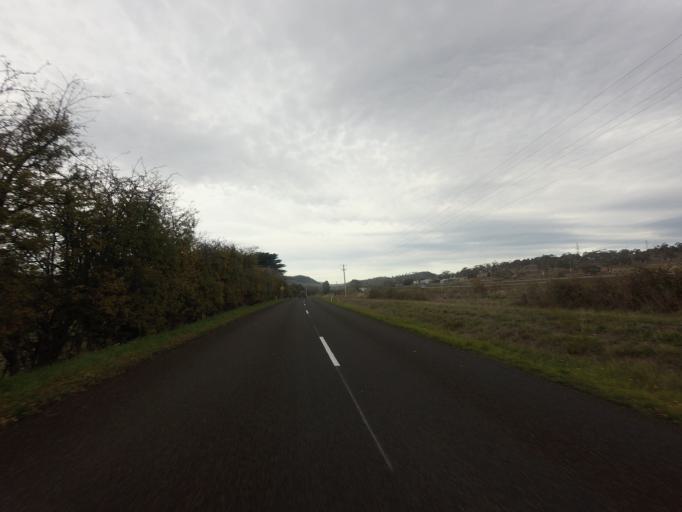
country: AU
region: Tasmania
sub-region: Brighton
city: Bridgewater
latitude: -42.6707
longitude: 147.1470
